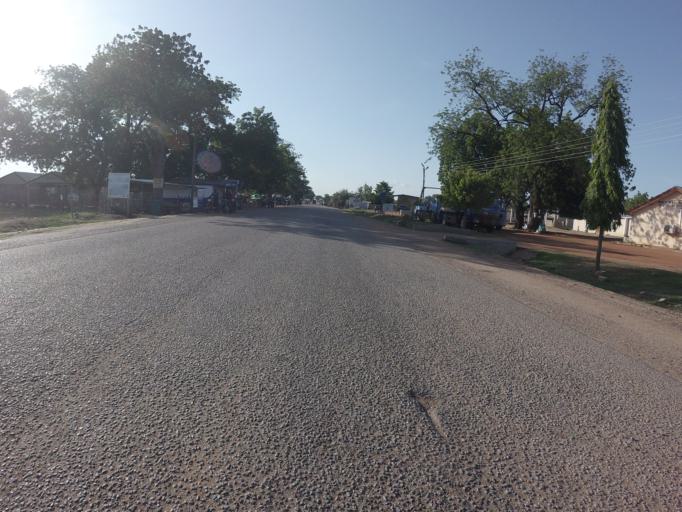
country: GH
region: Upper East
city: Navrongo
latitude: 10.9692
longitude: -1.1021
